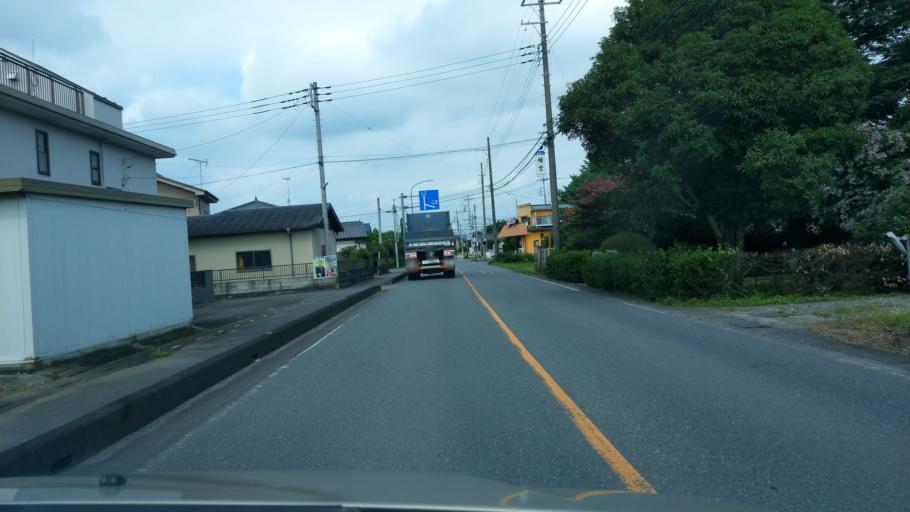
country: JP
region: Saitama
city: Sakado
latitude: 36.0321
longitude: 139.3498
